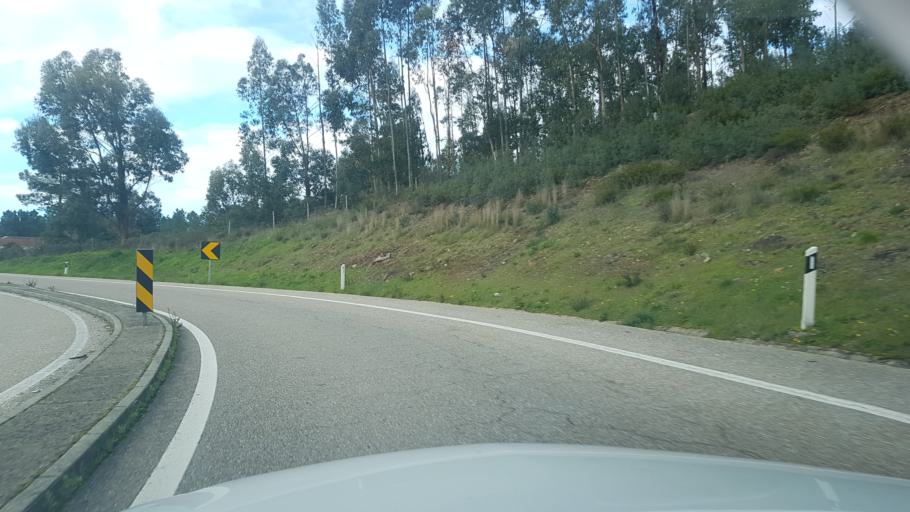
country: PT
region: Santarem
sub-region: Constancia
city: Constancia
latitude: 39.4841
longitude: -8.3532
